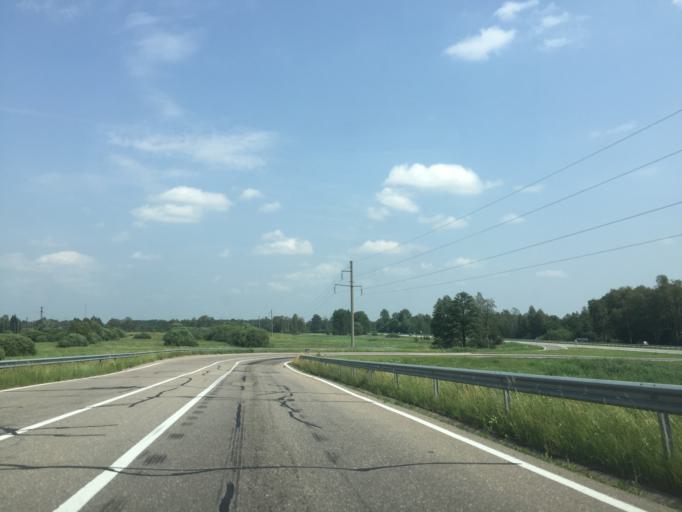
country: LV
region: Marupe
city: Marupe
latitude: 56.8359
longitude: 24.0404
